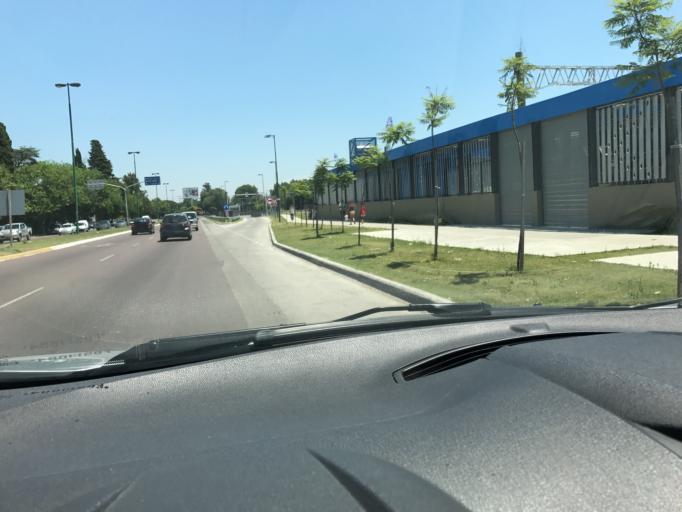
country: AR
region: Buenos Aires
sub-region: Partido de La Plata
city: La Plata
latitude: -34.8659
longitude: -58.0425
